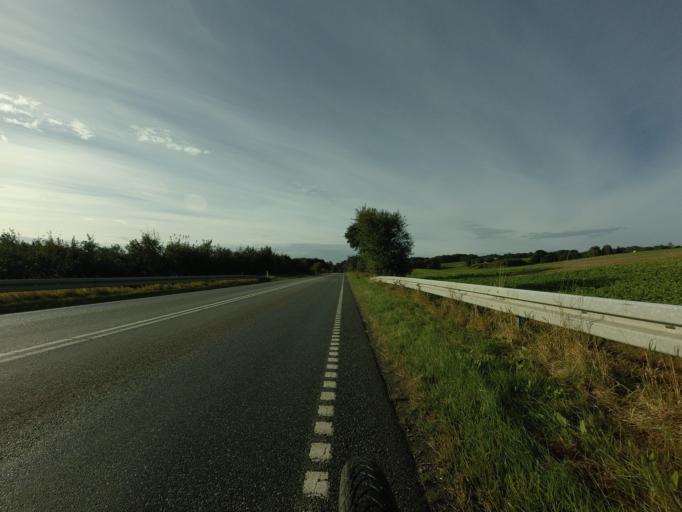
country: DK
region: Central Jutland
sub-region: Viborg Kommune
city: Bjerringbro
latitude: 56.4454
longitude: 9.5527
